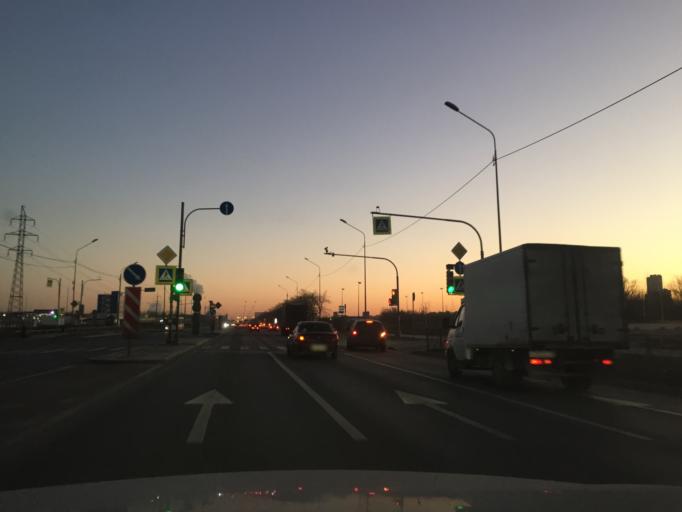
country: RU
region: St.-Petersburg
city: Obukhovo
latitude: 59.8590
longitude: 30.4207
